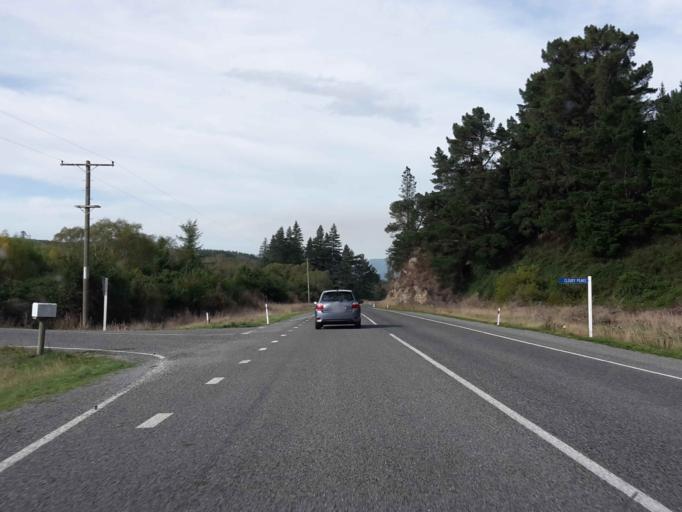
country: NZ
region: Canterbury
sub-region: Timaru District
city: Pleasant Point
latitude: -44.0297
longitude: 170.7129
